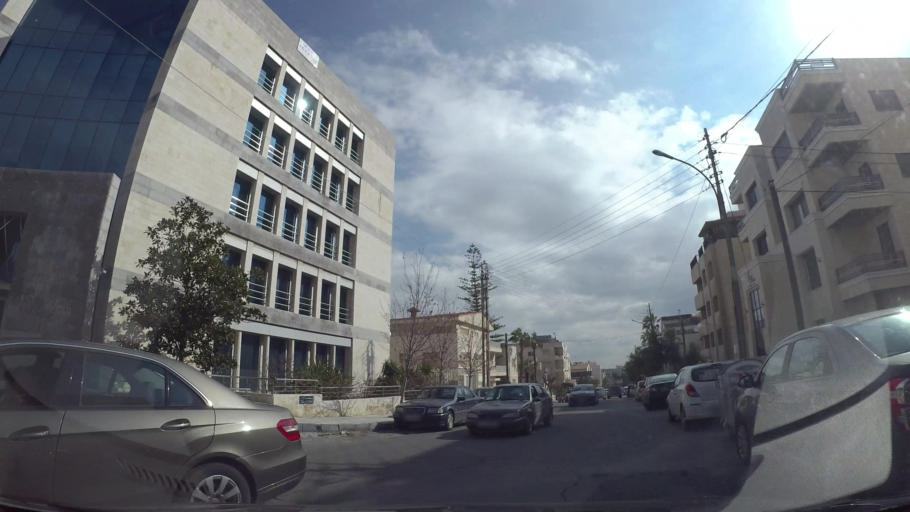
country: JO
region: Amman
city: Amman
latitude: 31.9705
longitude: 35.8920
